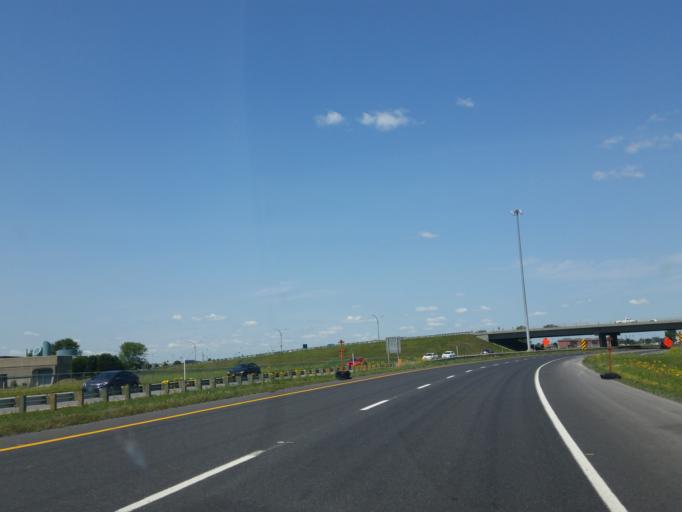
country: CA
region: Quebec
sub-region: Monteregie
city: Saint-Jean-sur-Richelieu
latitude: 45.3292
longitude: -73.2860
